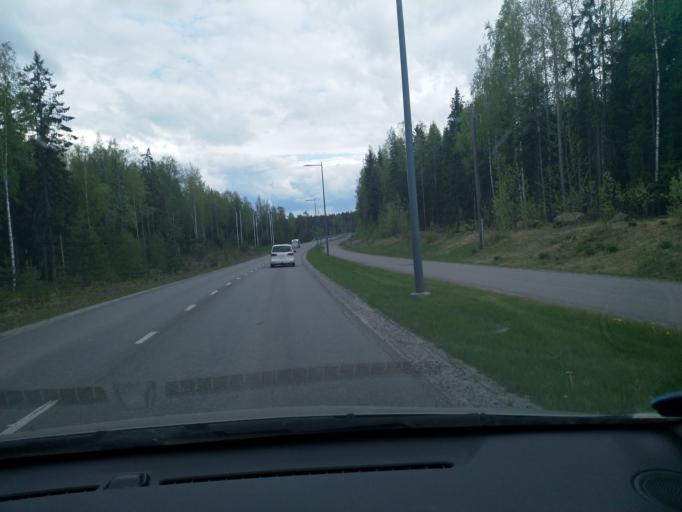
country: FI
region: Pirkanmaa
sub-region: Tampere
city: Tampere
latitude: 61.4520
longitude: 23.8015
